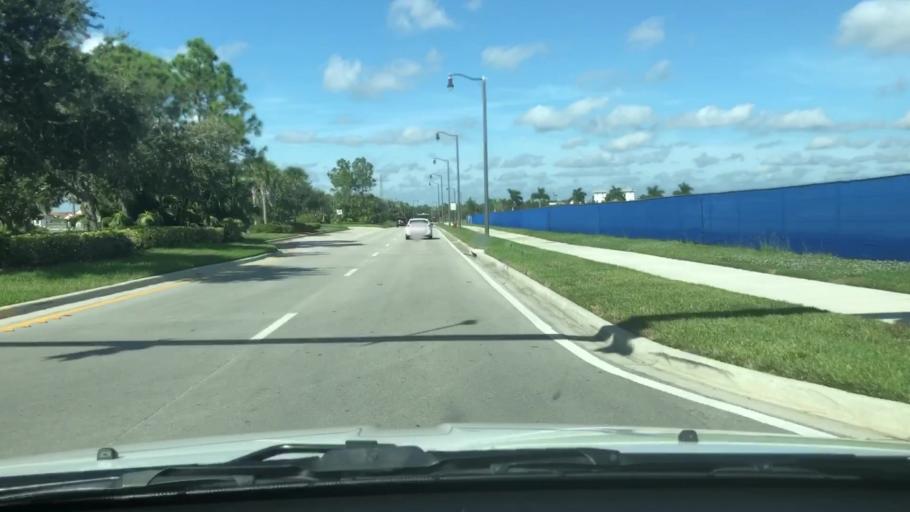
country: US
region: Florida
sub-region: Saint Lucie County
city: Port Saint Lucie
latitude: 27.2735
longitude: -80.4303
